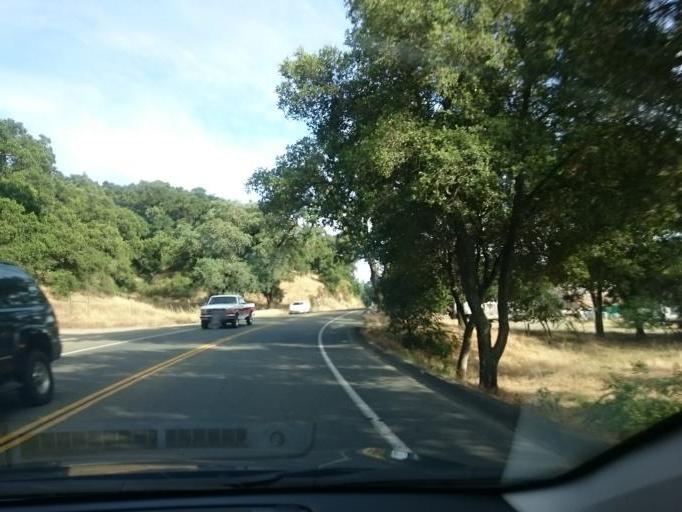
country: US
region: California
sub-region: Napa County
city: Saint Helena
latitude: 38.5038
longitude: -122.4343
